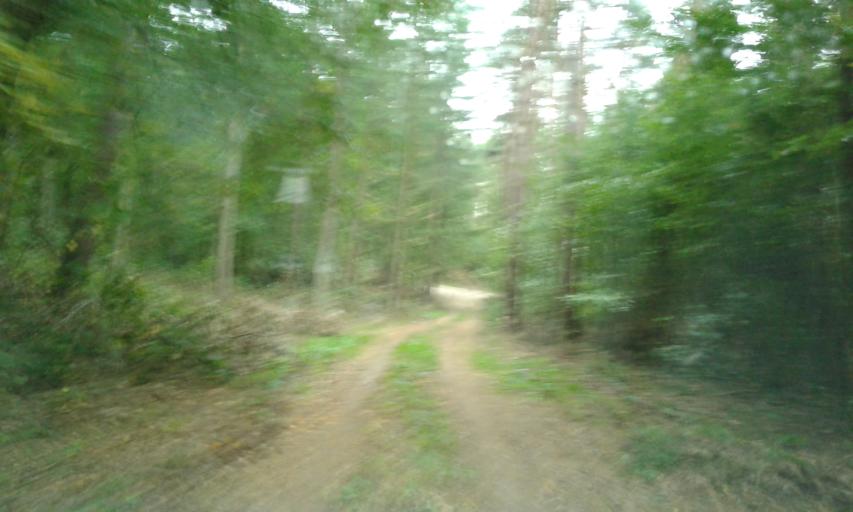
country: PL
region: West Pomeranian Voivodeship
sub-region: Powiat choszczenski
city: Pelczyce
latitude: 53.0885
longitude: 15.2260
